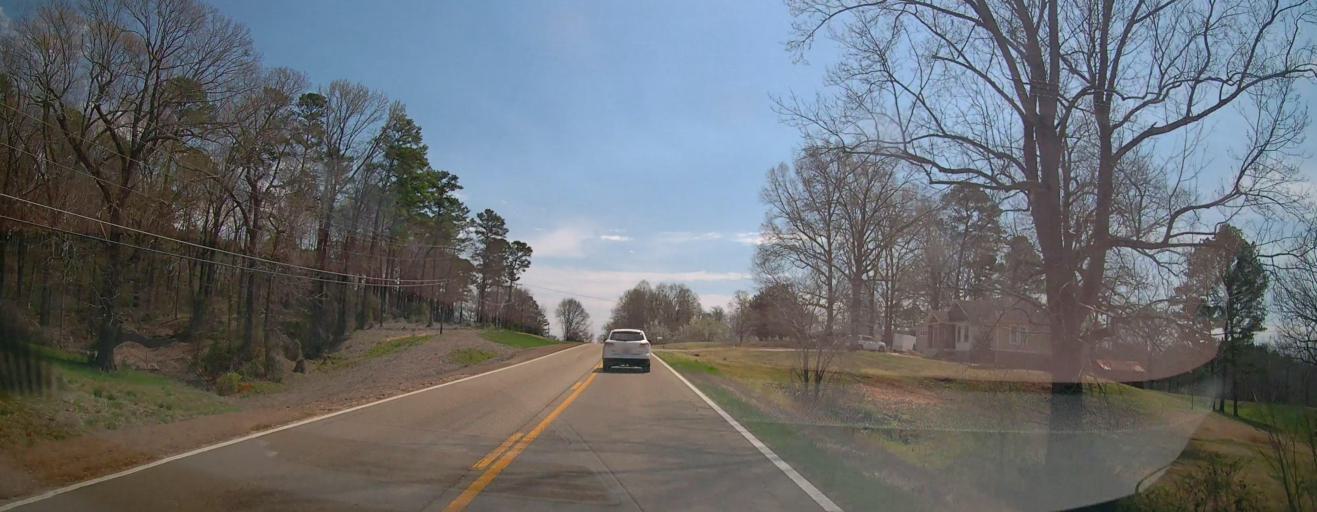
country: US
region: Mississippi
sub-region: Union County
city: New Albany
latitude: 34.4498
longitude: -88.9701
